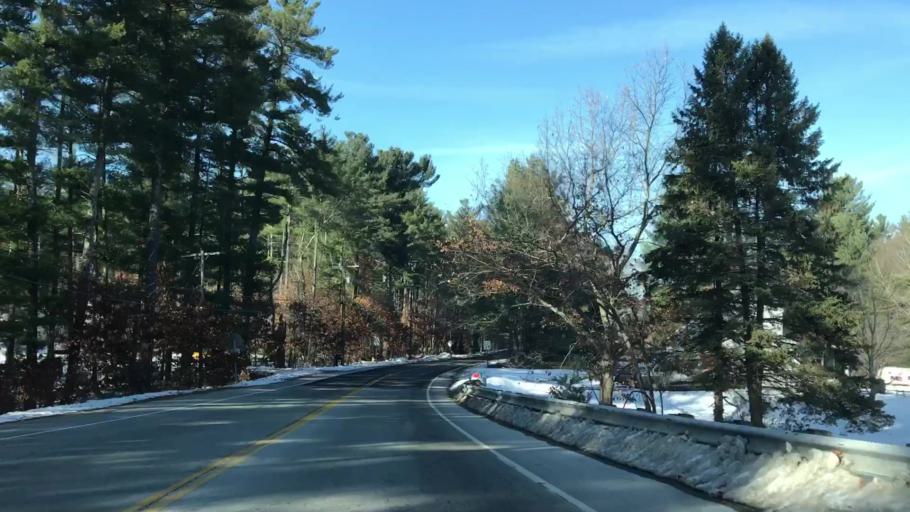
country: US
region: New Hampshire
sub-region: Hillsborough County
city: Milford
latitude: 42.8232
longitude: -71.6064
